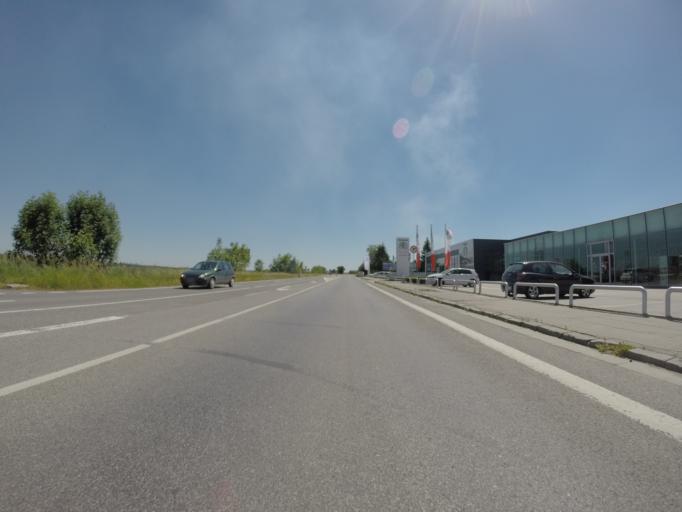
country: SK
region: Trnavsky
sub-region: Okres Galanta
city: Galanta
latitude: 48.1931
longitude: 17.7433
